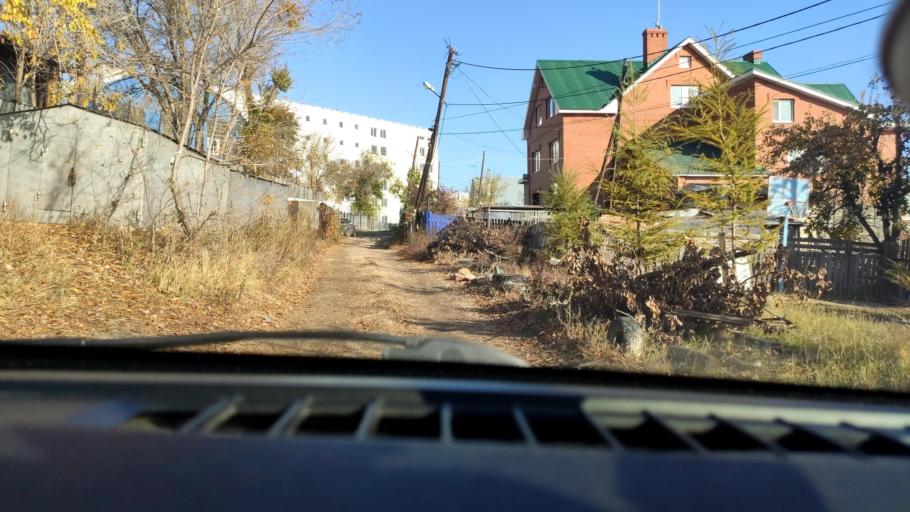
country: RU
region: Samara
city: Samara
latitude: 53.1839
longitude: 50.1992
